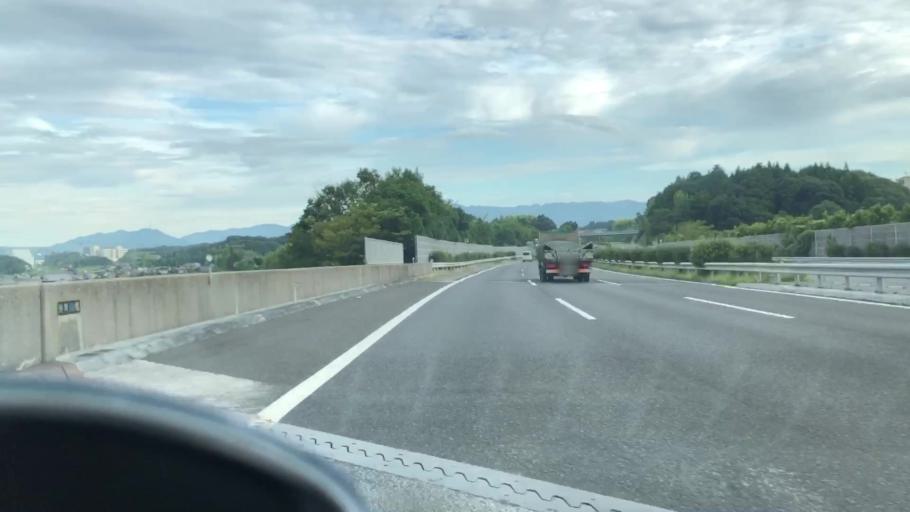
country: JP
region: Hyogo
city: Sandacho
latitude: 34.8751
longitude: 135.1952
